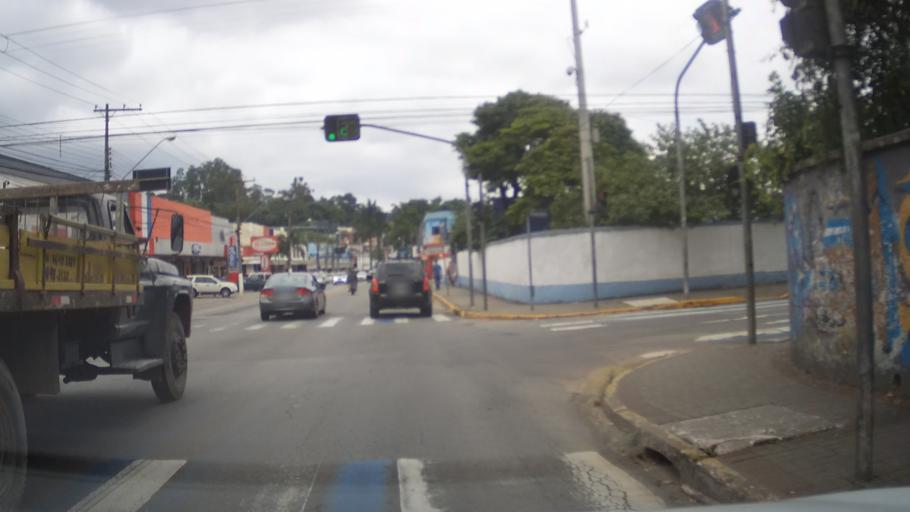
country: BR
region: Sao Paulo
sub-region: Aruja
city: Aruja
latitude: -23.3943
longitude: -46.3212
